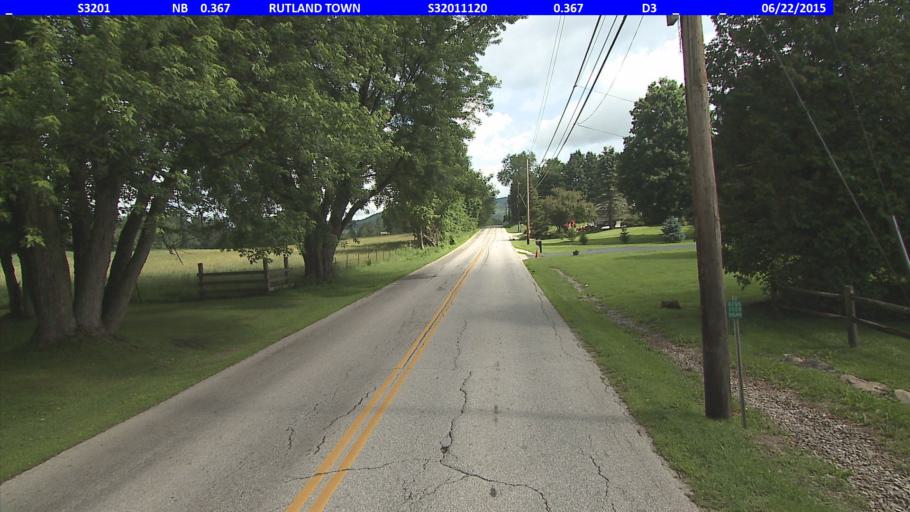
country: US
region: Vermont
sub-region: Rutland County
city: Rutland
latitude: 43.6432
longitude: -72.9745
